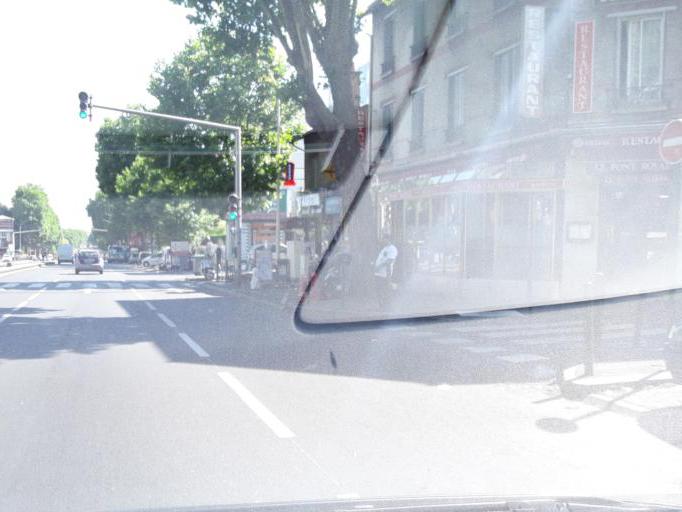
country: FR
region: Ile-de-France
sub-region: Departement du Val-de-Marne
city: Arcueil
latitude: 48.7950
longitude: 2.3213
